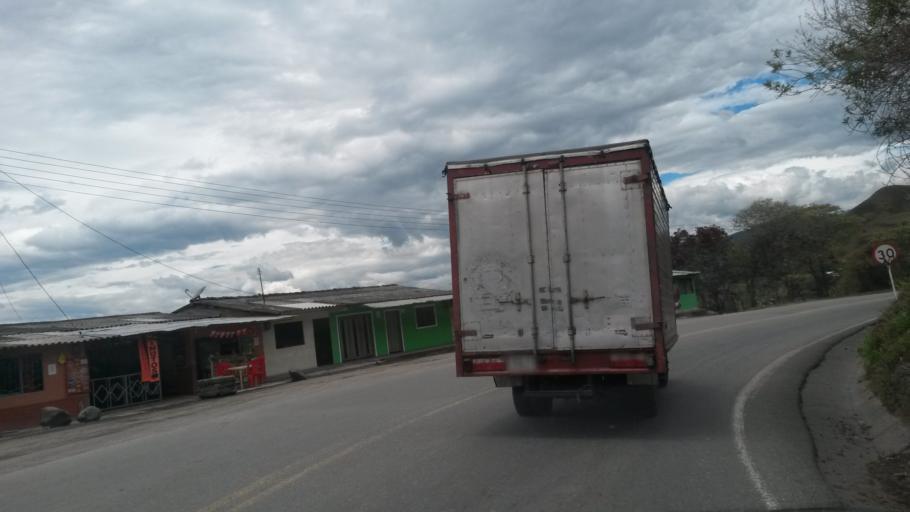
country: CO
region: Cauca
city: Rosas
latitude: 2.2661
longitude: -76.7385
